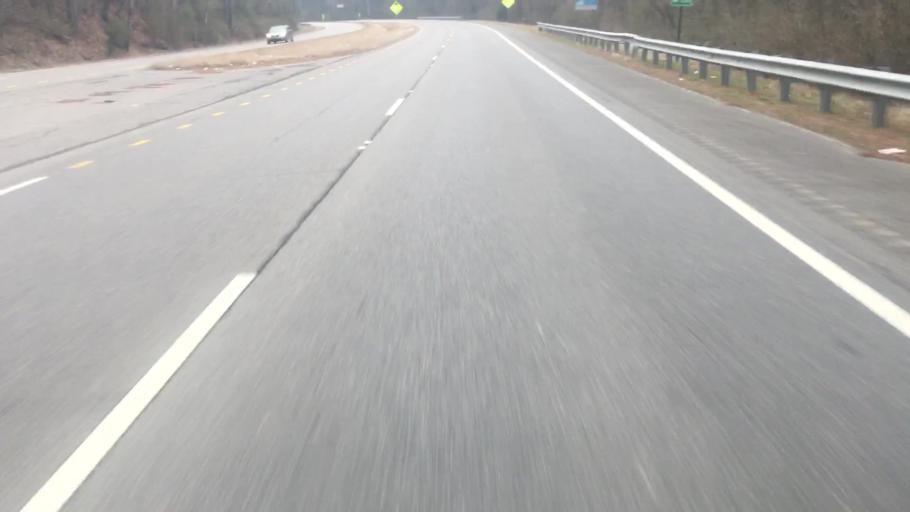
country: US
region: Alabama
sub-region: Walker County
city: Cordova
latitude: 33.8222
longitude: -87.1888
